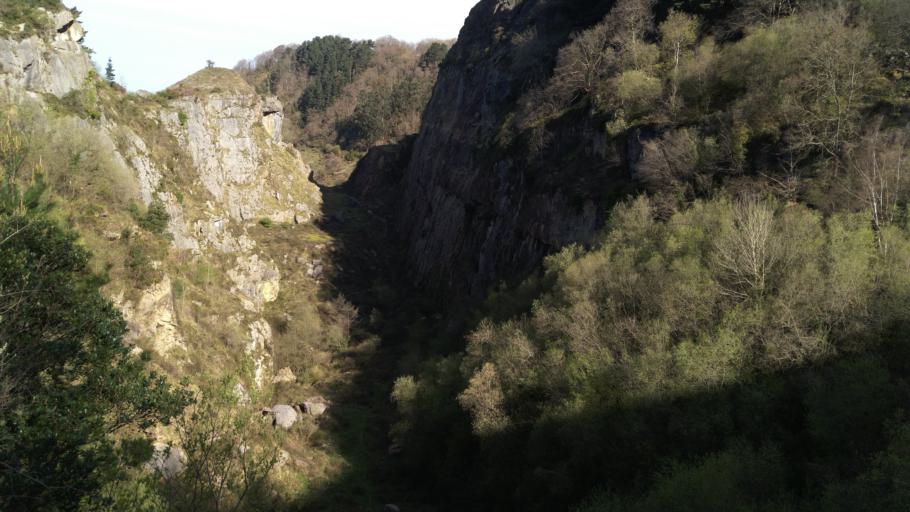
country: ES
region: Basque Country
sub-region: Bizkaia
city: El Corrillo
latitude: 43.2686
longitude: -3.0978
